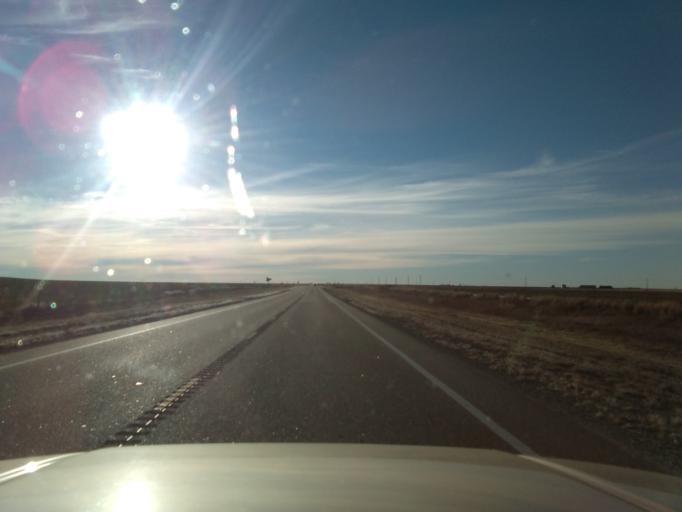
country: US
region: Kansas
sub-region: Sheridan County
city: Hoxie
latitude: 39.5123
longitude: -100.6413
